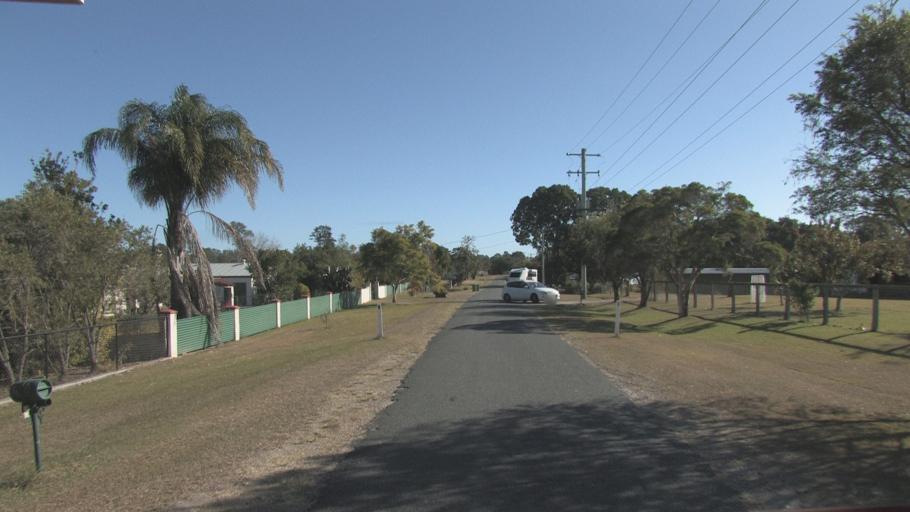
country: AU
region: Queensland
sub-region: Logan
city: North Maclean
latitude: -27.7847
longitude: 153.0035
